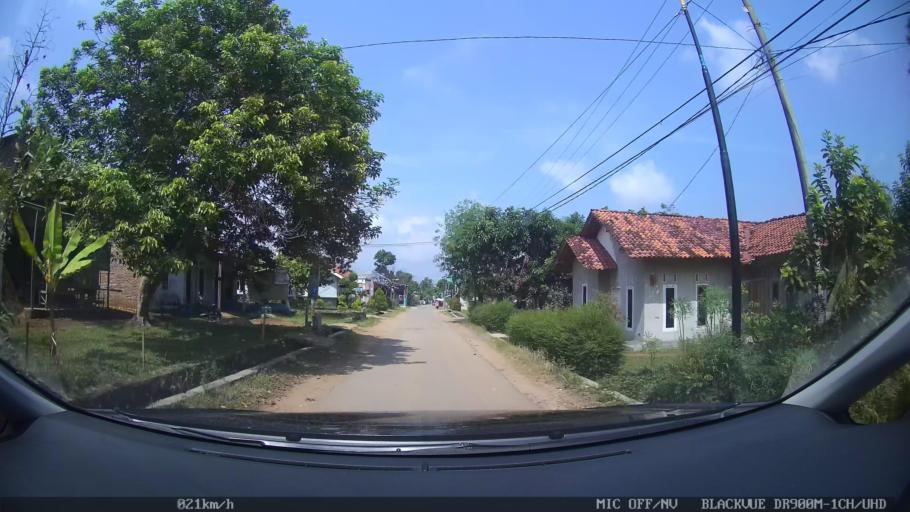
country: ID
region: Lampung
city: Kedaton
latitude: -5.3450
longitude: 105.2914
